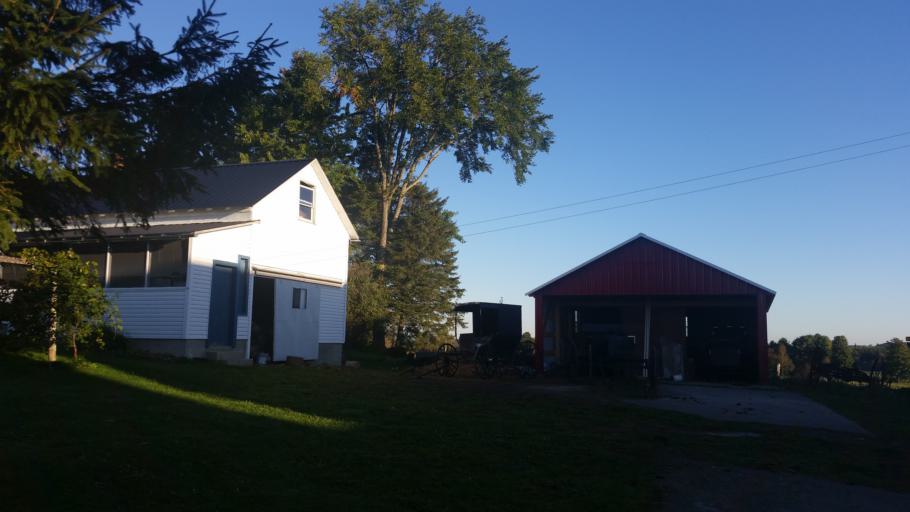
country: US
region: Maine
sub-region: Aroostook County
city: Fort Fairfield
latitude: 46.6964
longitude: -67.8467
